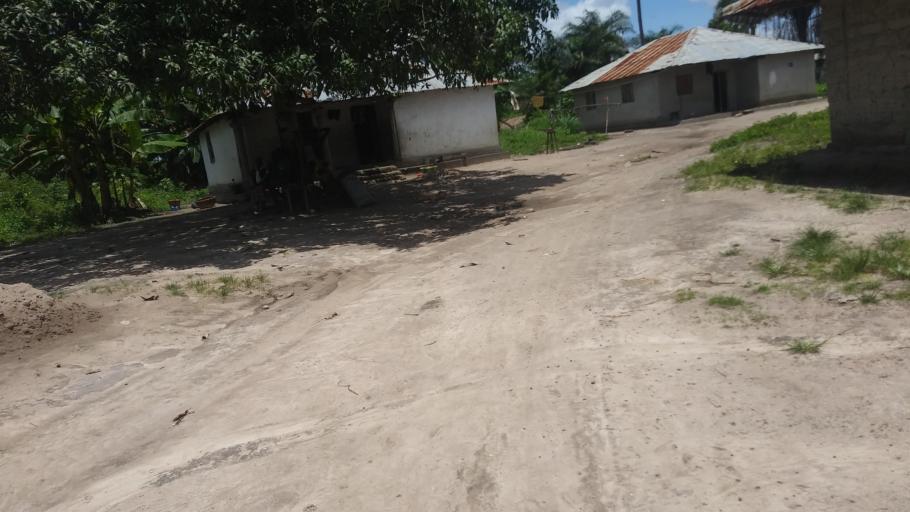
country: SL
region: Northern Province
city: Makeni
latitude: 8.8861
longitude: -12.0170
